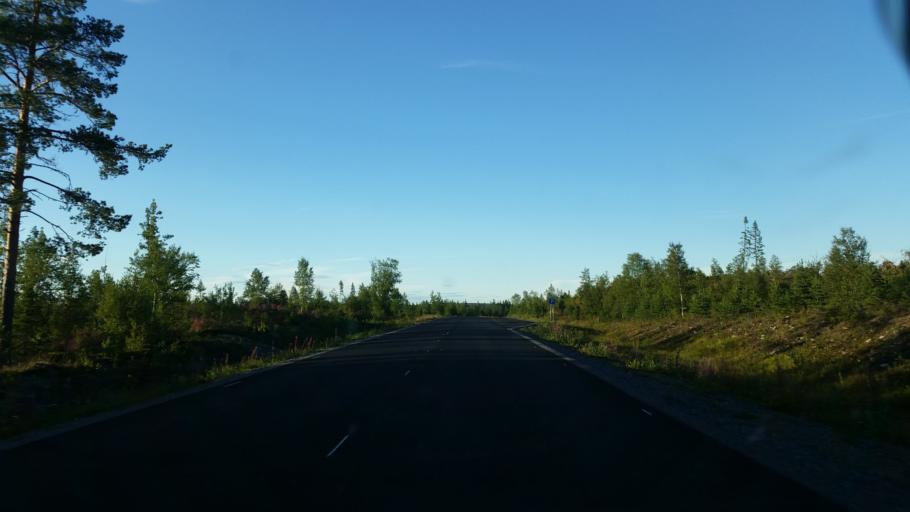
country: SE
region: Vaesterbotten
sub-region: Dorotea Kommun
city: Dorotea
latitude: 64.3164
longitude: 16.6093
